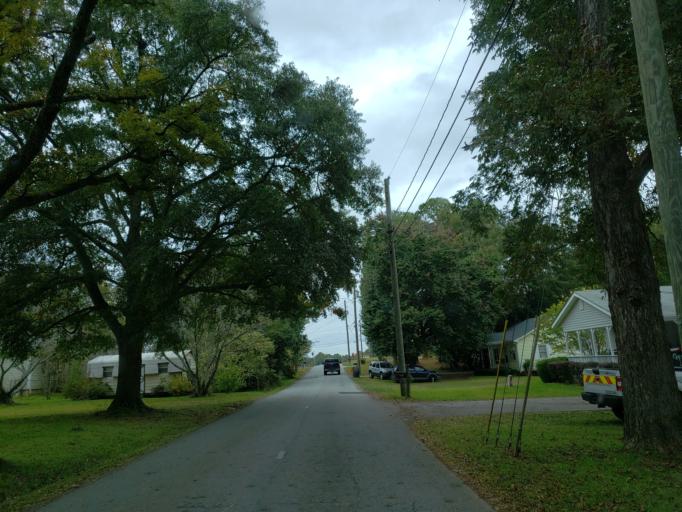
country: US
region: Georgia
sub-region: Monroe County
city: Forsyth
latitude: 33.0335
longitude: -83.9273
